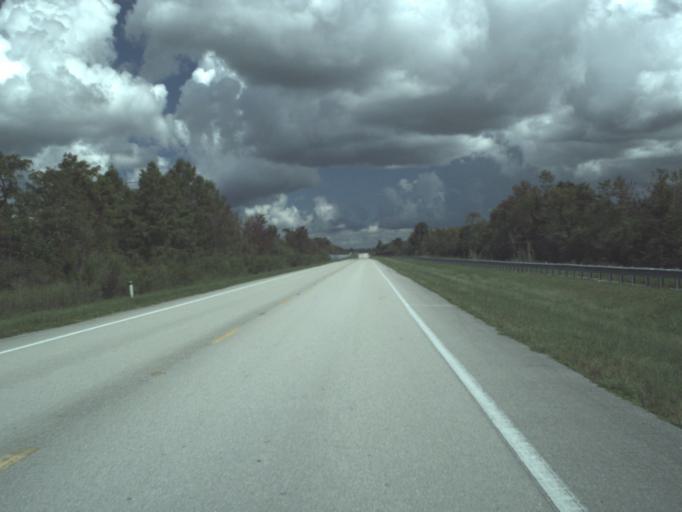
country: US
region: Florida
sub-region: Collier County
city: Lely Resort
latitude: 25.9714
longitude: -81.3518
